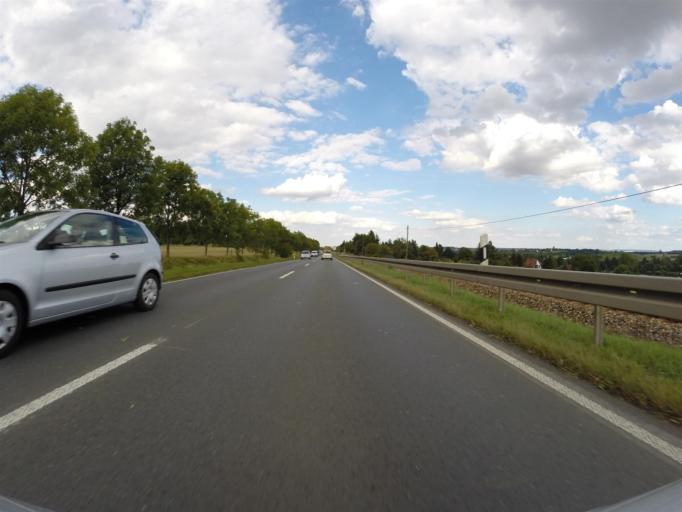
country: DE
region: Thuringia
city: Hopfgarten
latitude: 50.9757
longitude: 11.2835
